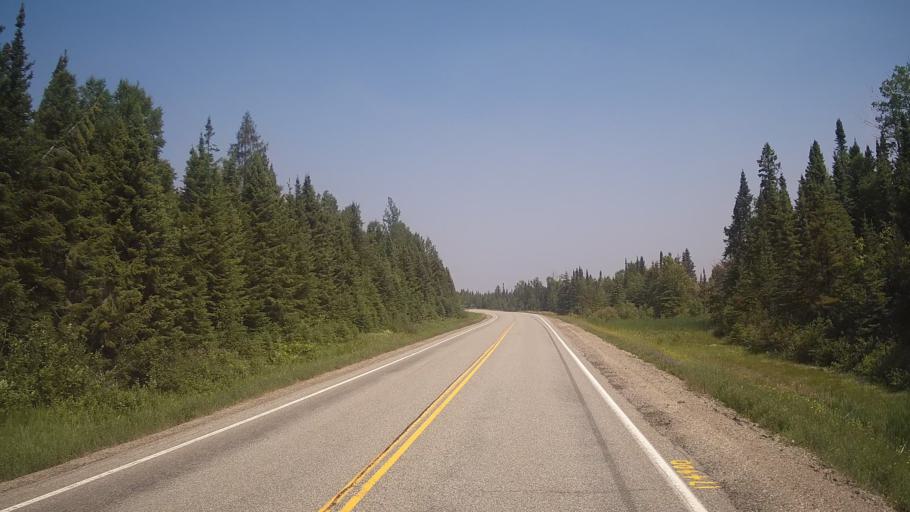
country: CA
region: Ontario
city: Timmins
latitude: 48.1690
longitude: -81.5831
